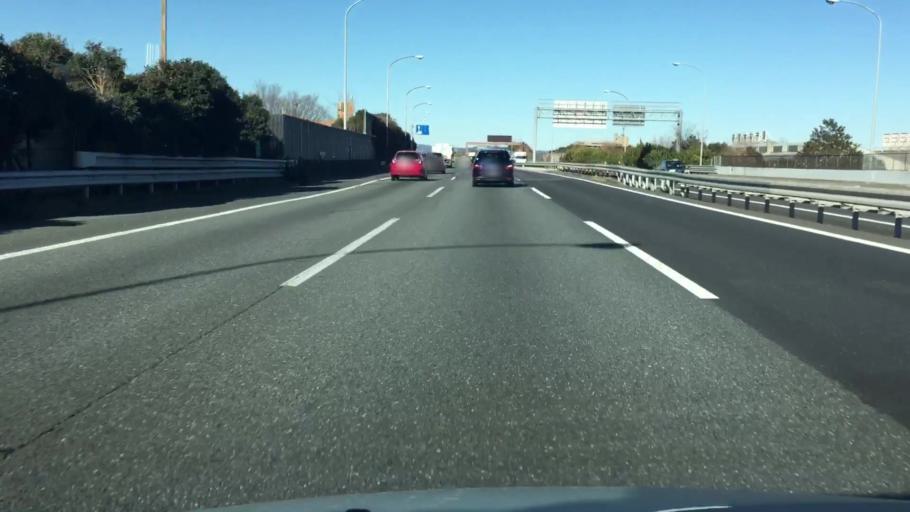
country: JP
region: Saitama
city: Sakado
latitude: 35.9480
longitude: 139.3962
